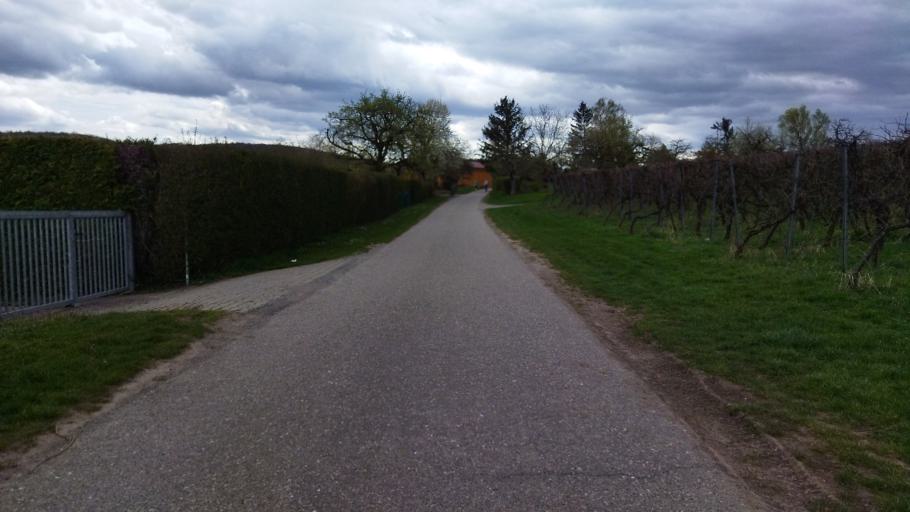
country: DE
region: Baden-Wuerttemberg
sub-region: Regierungsbezirk Stuttgart
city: Erlenbach
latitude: 49.1869
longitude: 9.2650
